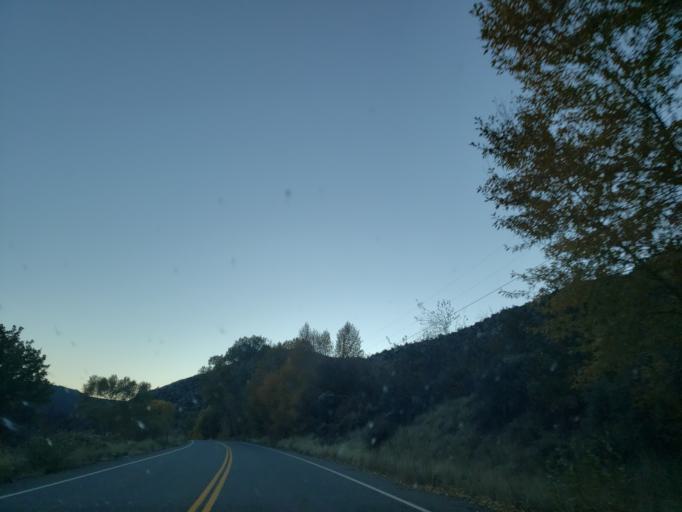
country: US
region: Colorado
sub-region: Garfield County
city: New Castle
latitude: 39.5677
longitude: -107.5479
